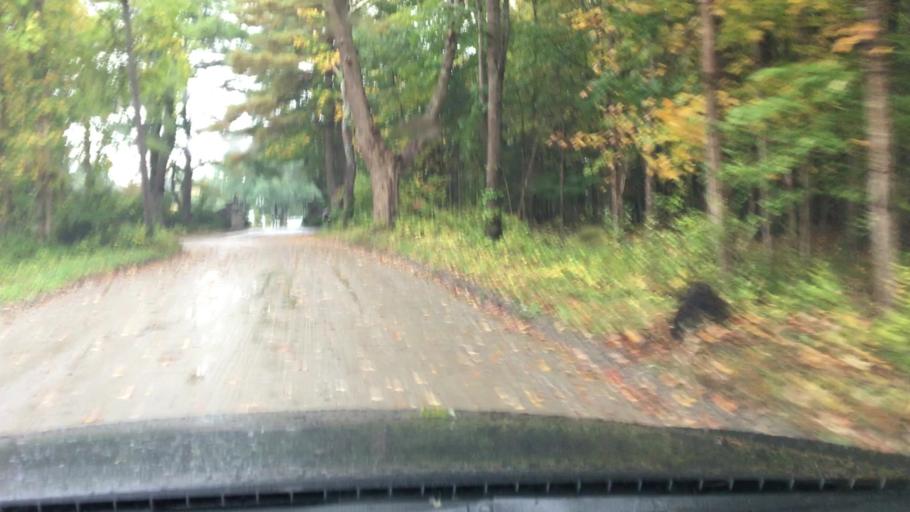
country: US
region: Connecticut
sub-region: Litchfield County
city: New Milford
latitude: 41.5813
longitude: -73.3935
